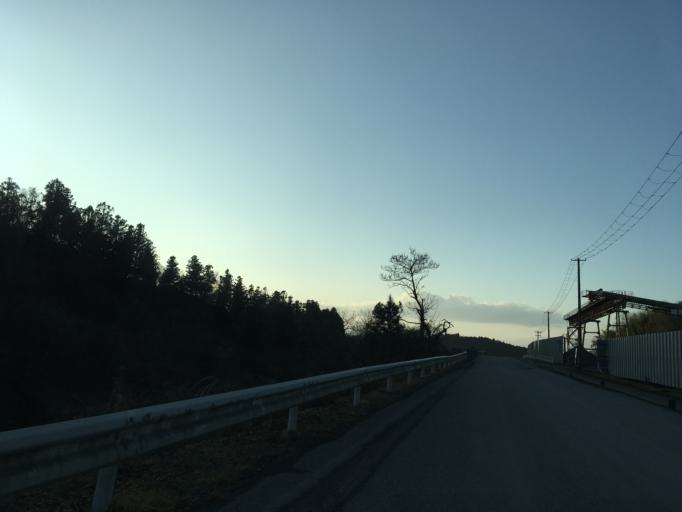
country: JP
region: Iwate
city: Ichinoseki
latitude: 38.8054
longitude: 141.2235
